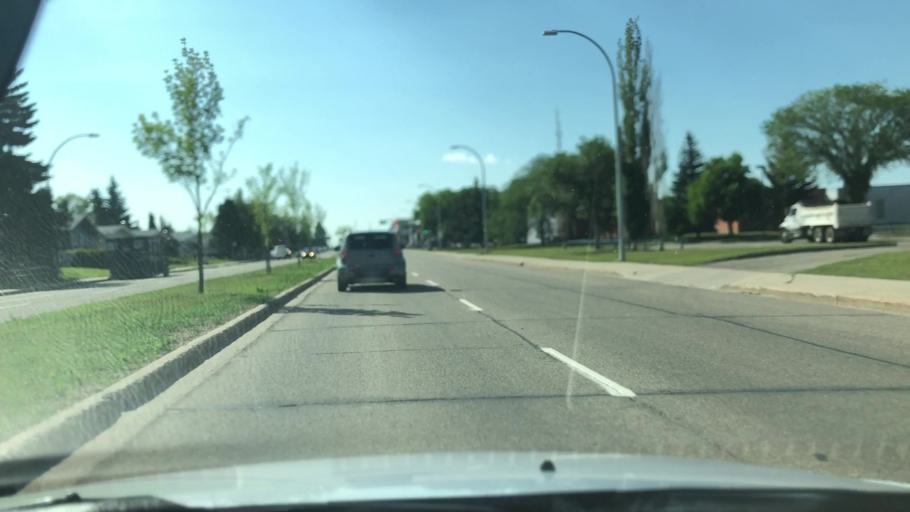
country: CA
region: Alberta
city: Edmonton
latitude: 53.6052
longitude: -113.4478
